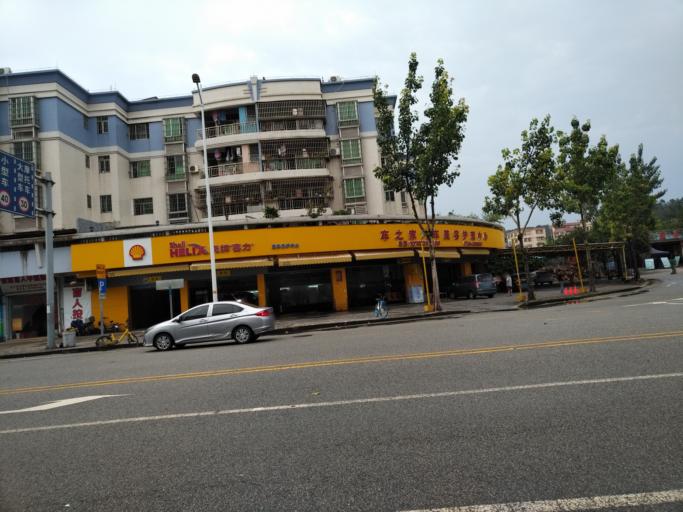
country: CN
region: Guangdong
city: Jianghai
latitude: 22.5744
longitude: 113.1110
